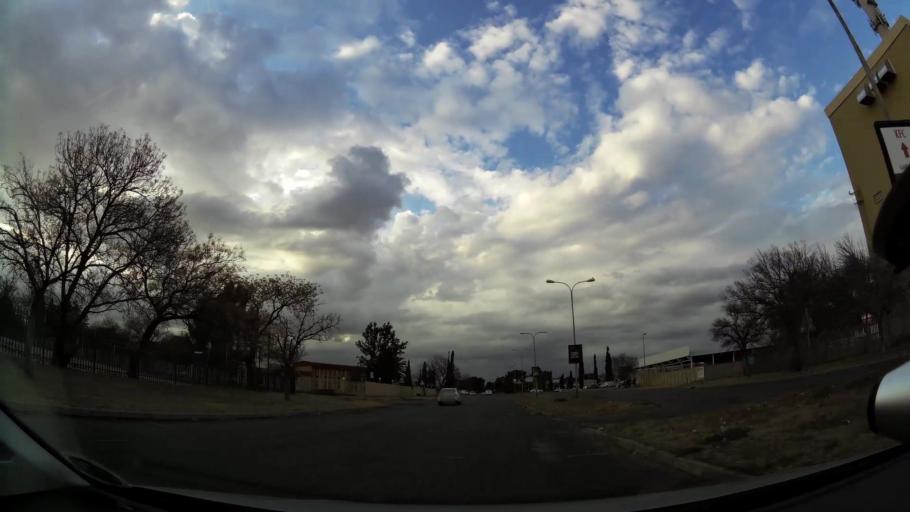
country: ZA
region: Orange Free State
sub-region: Lejweleputswa District Municipality
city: Welkom
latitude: -27.9799
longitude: 26.7312
